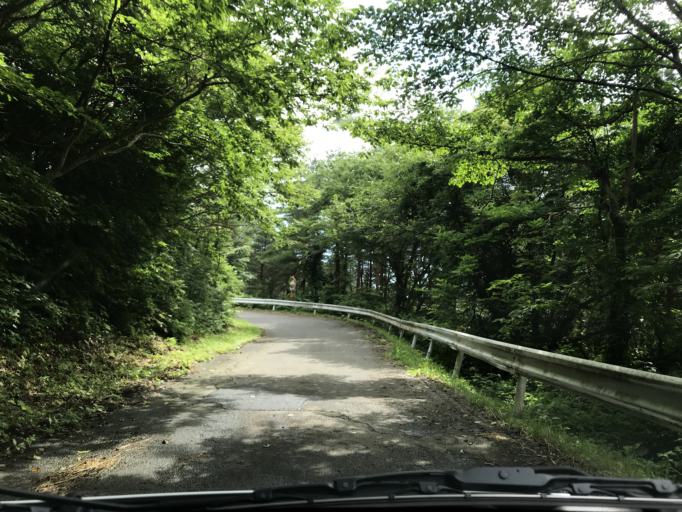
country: JP
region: Iwate
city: Ofunato
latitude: 38.9859
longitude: 141.4424
